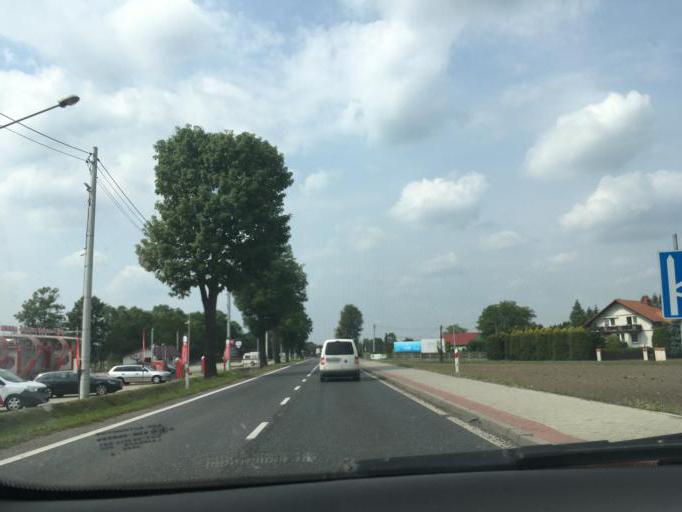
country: PL
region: Silesian Voivodeship
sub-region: Powiat bierunsko-ledzinski
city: Bierun
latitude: 50.0839
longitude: 19.1313
